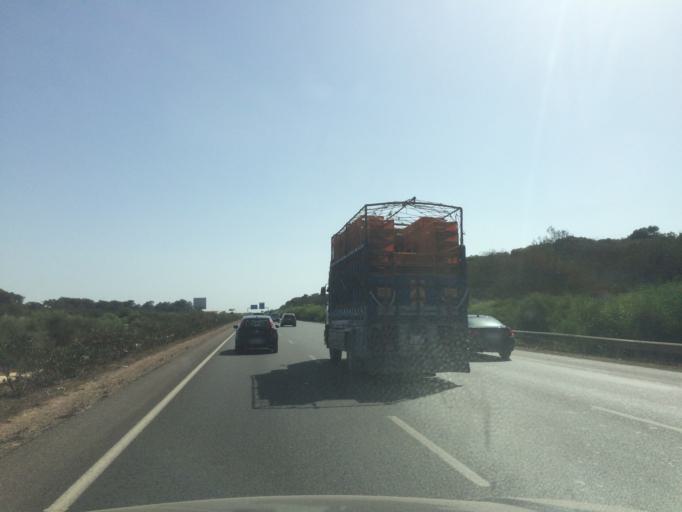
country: MA
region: Rabat-Sale-Zemmour-Zaer
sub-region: Skhirate-Temara
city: Temara
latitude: 33.9418
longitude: -6.9265
